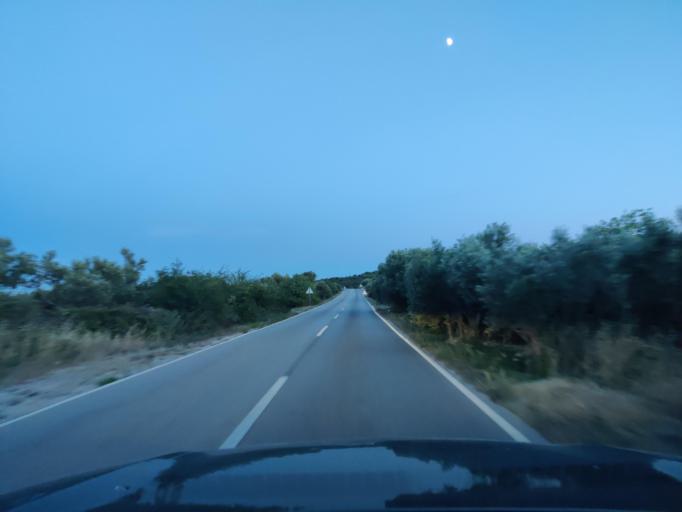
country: HR
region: Sibensko-Kniniska
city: Murter
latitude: 43.8142
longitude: 15.6011
